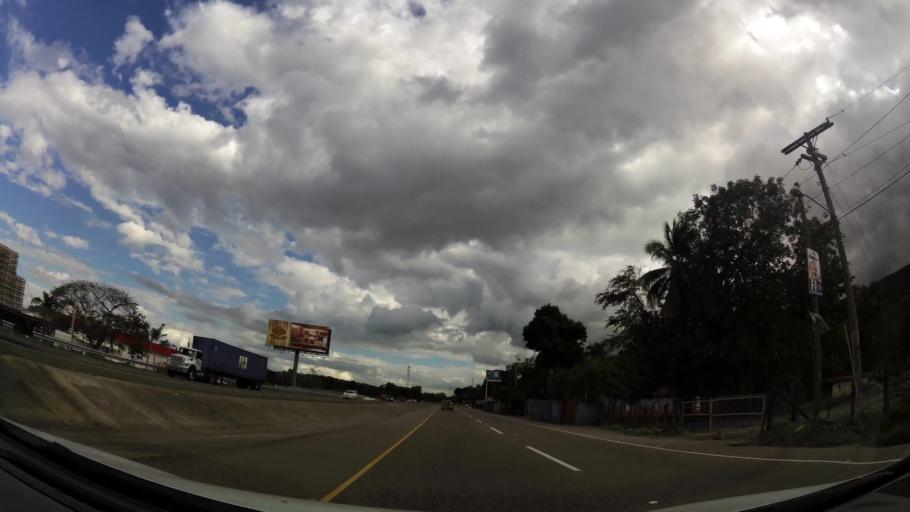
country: DO
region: La Vega
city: Rincon
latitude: 19.1520
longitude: -70.4789
